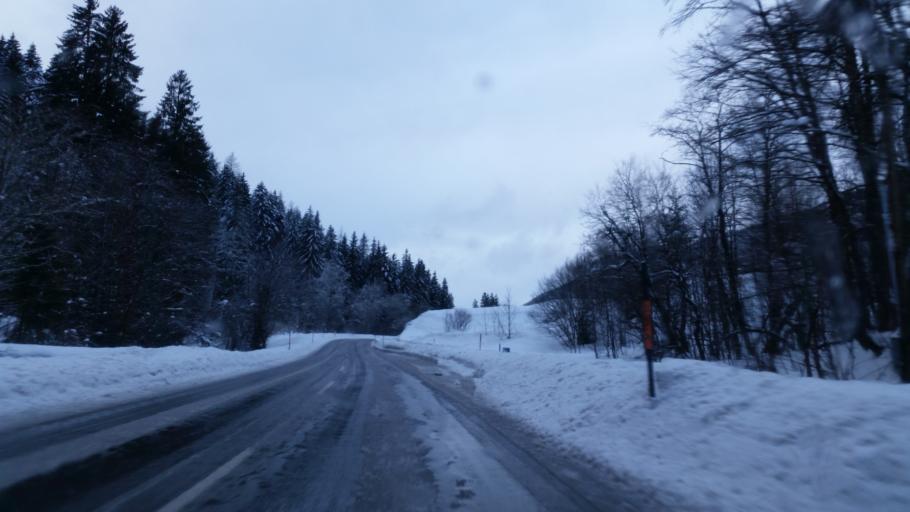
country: AT
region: Salzburg
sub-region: Politischer Bezirk Zell am See
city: Leogang
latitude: 47.4467
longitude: 12.6908
